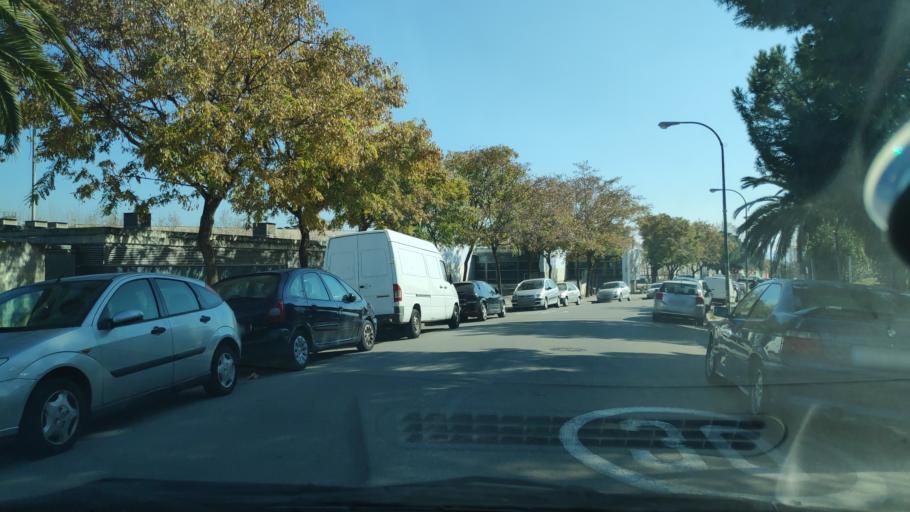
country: ES
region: Catalonia
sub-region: Provincia de Barcelona
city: Sant Quirze del Valles
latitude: 41.5456
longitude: 2.0903
